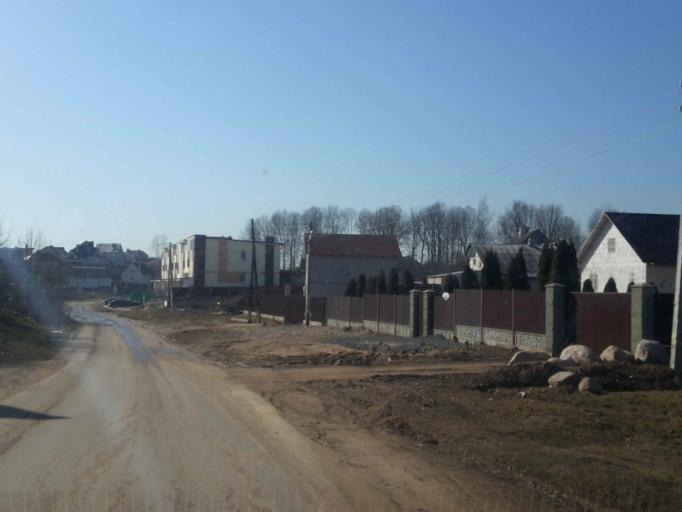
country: BY
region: Minsk
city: Zhdanovichy
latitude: 53.9226
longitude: 27.4022
